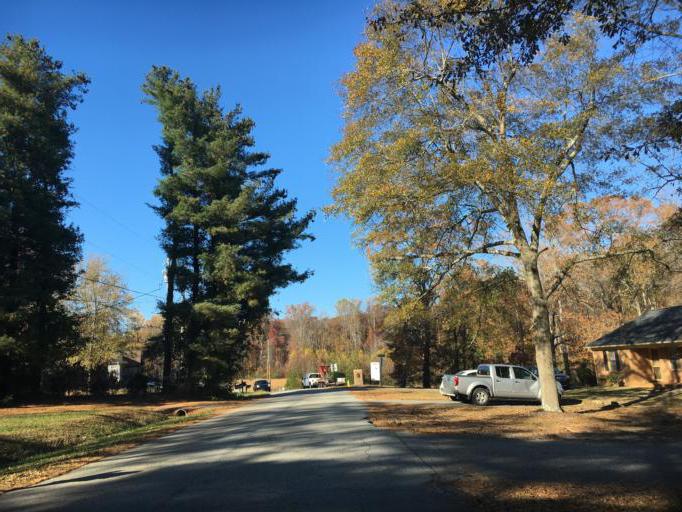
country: US
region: South Carolina
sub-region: Spartanburg County
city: Inman Mills
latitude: 35.0534
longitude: -82.1070
